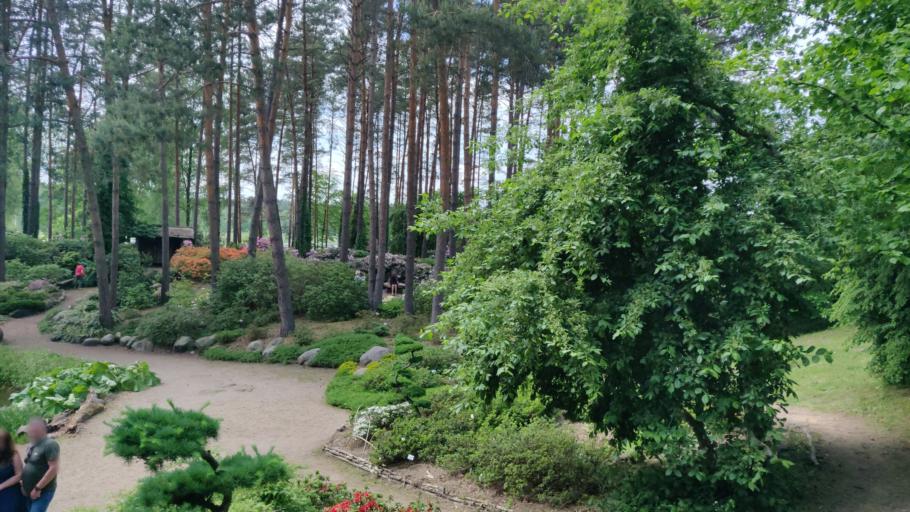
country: LT
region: Vilnius County
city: Rasos
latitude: 54.7350
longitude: 25.3996
